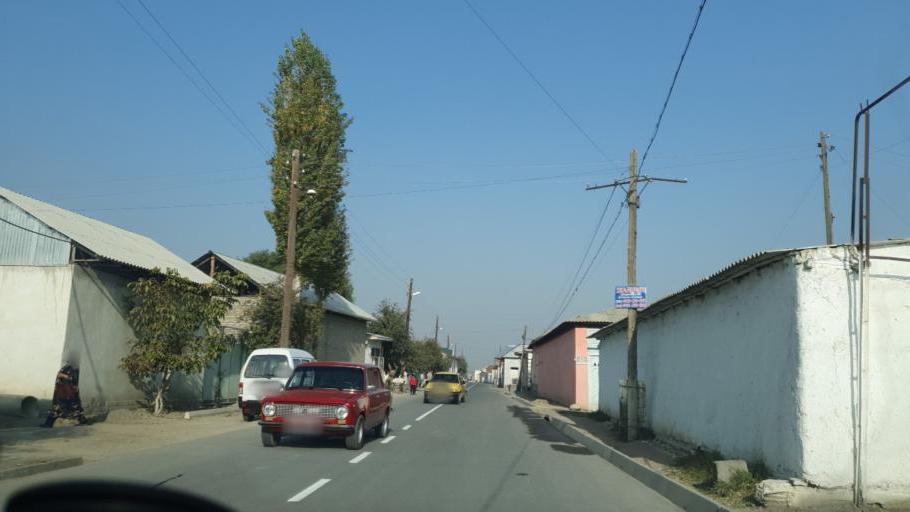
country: UZ
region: Fergana
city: Qo`qon
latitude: 40.5839
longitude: 70.9085
